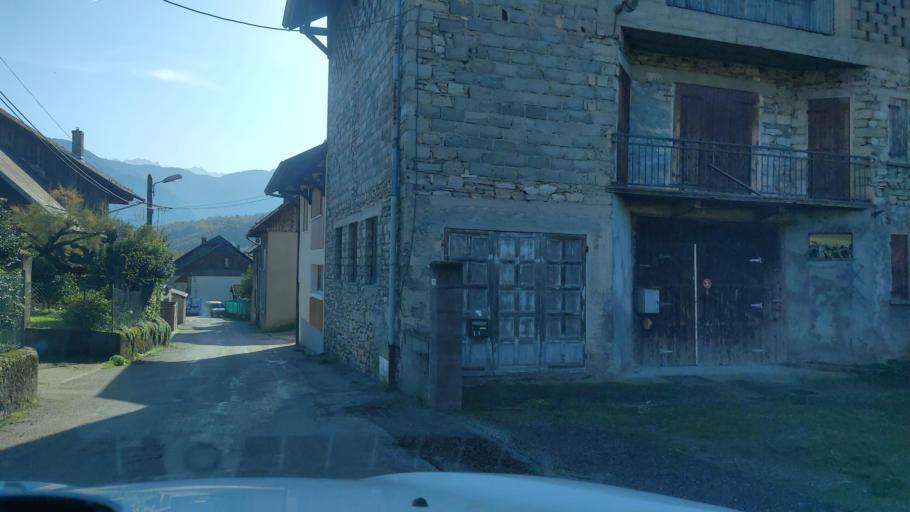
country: FR
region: Rhone-Alpes
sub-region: Departement de la Savoie
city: Coise-Saint-Jean-Pied-Gauthier
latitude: 45.5619
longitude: 6.1710
